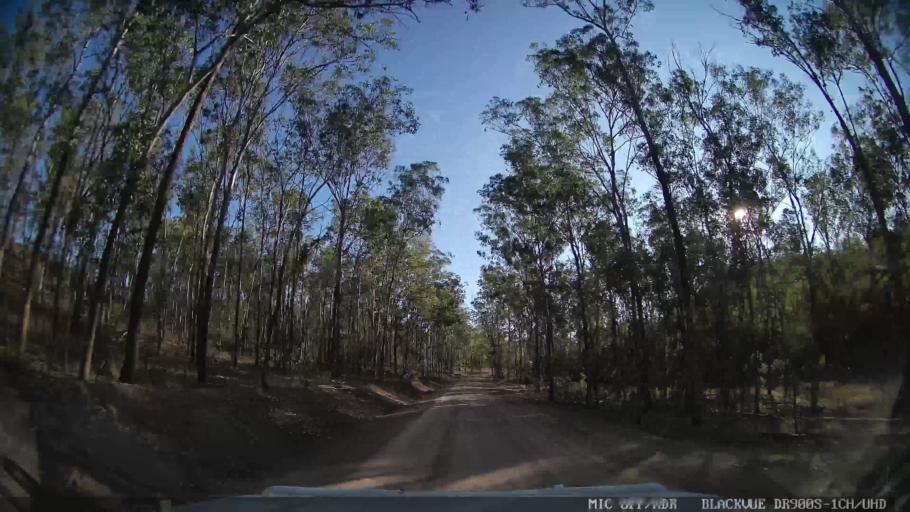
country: AU
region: Queensland
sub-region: Gladstone
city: Toolooa
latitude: -24.6951
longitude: 151.4100
